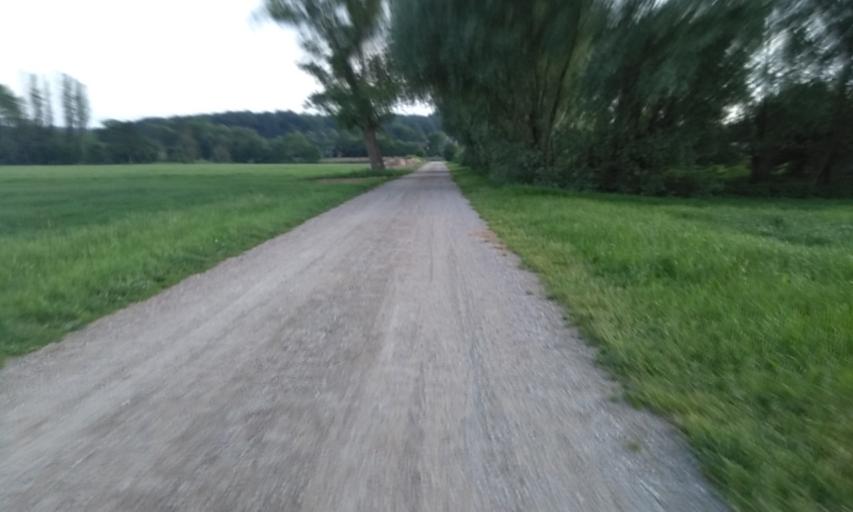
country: DE
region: Lower Saxony
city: Nottensdorf
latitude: 53.4876
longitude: 9.6319
